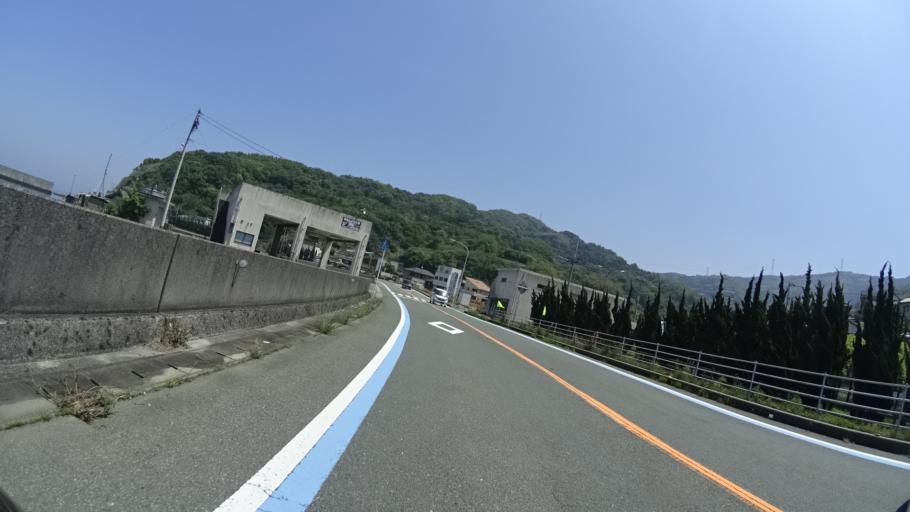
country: JP
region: Ehime
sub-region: Nishiuwa-gun
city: Ikata-cho
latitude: 33.5726
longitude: 132.4412
